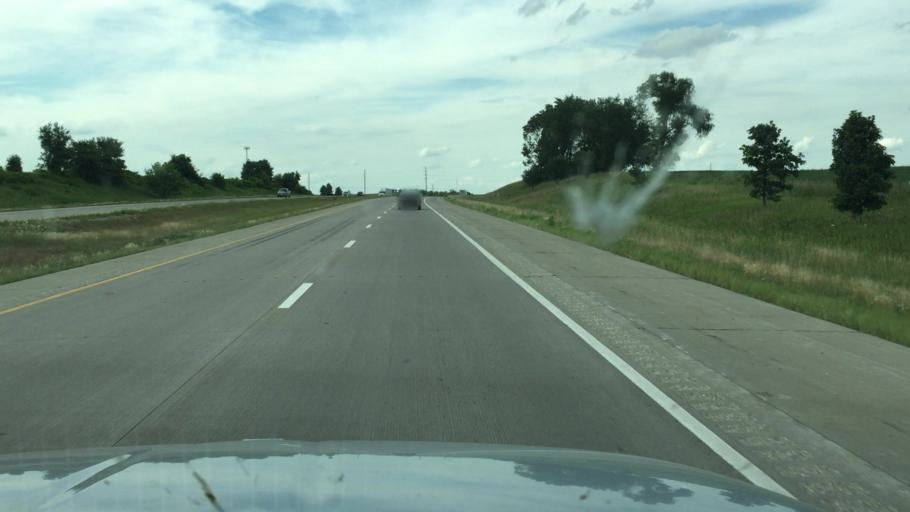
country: US
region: Iowa
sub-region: Scott County
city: Walcott
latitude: 41.5641
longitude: -90.6787
